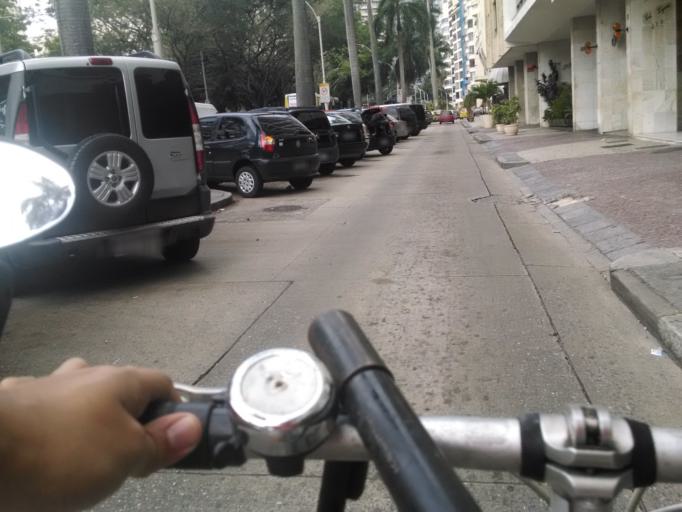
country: BR
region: Rio de Janeiro
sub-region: Rio De Janeiro
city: Rio de Janeiro
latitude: -22.9358
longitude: -43.1743
